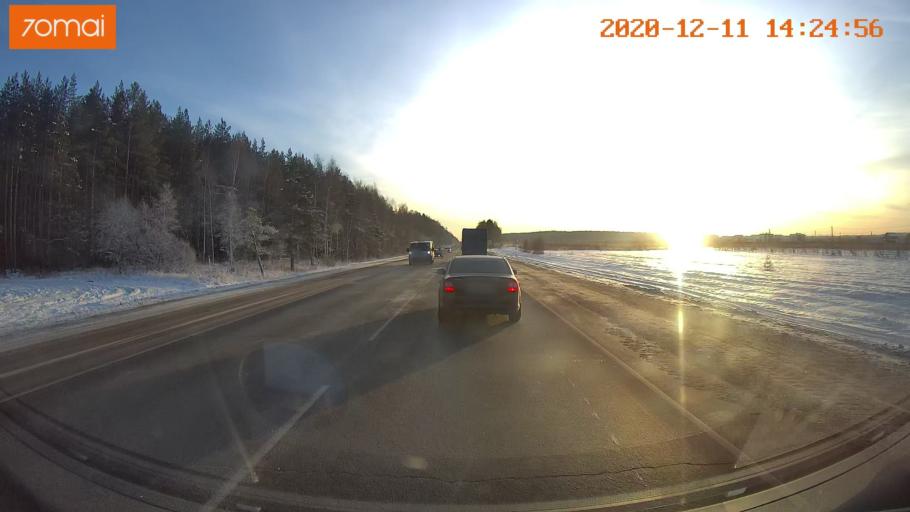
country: RU
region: Kostroma
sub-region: Kostromskoy Rayon
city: Kostroma
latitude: 57.7151
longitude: 40.8941
